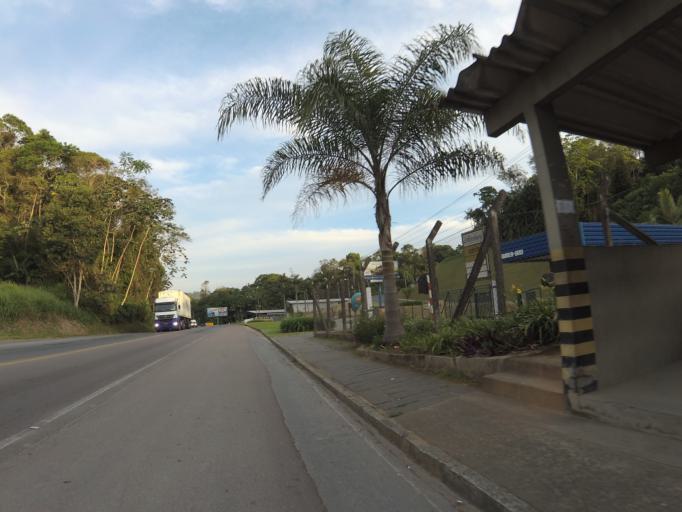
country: BR
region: Santa Catarina
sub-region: Indaial
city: Indaial
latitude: -26.8833
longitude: -49.1526
